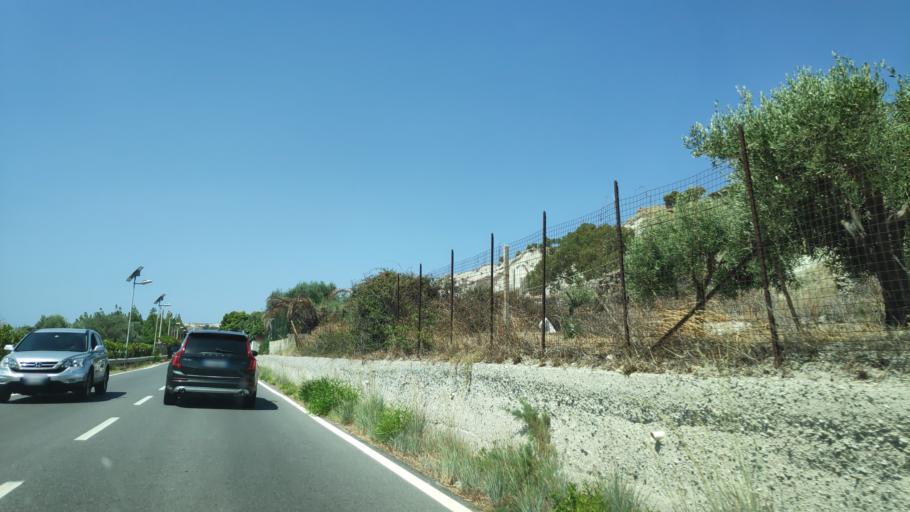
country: IT
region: Calabria
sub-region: Provincia di Reggio Calabria
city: Palizzi Marina
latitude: 37.9233
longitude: 16.0201
